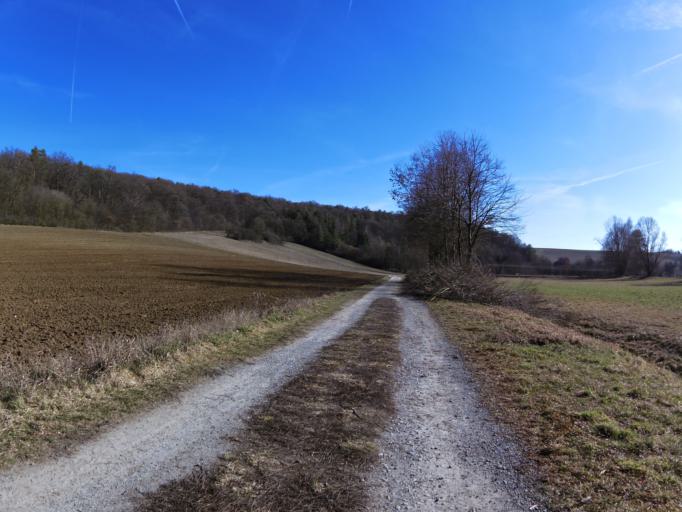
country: DE
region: Bavaria
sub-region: Regierungsbezirk Unterfranken
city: Rimpar
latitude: 49.8544
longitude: 9.9824
